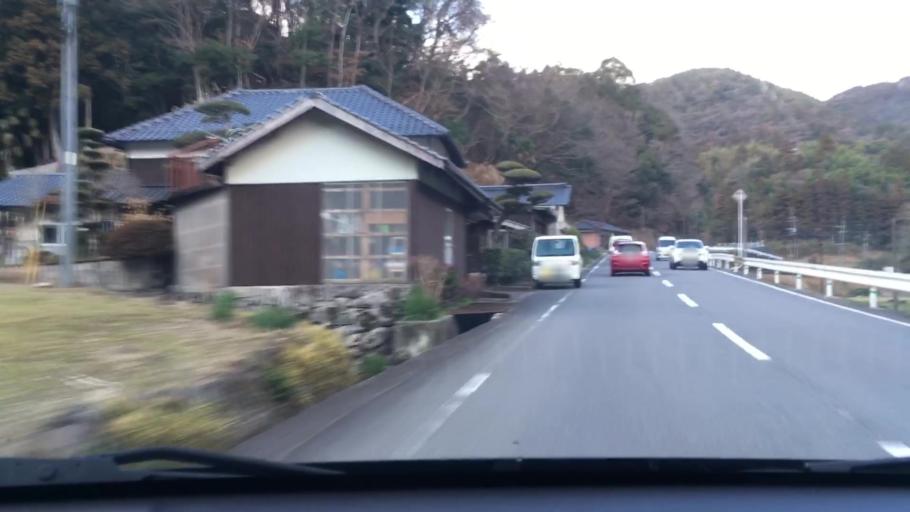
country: JP
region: Oita
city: Bungo-Takada-shi
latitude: 33.4651
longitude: 131.3881
